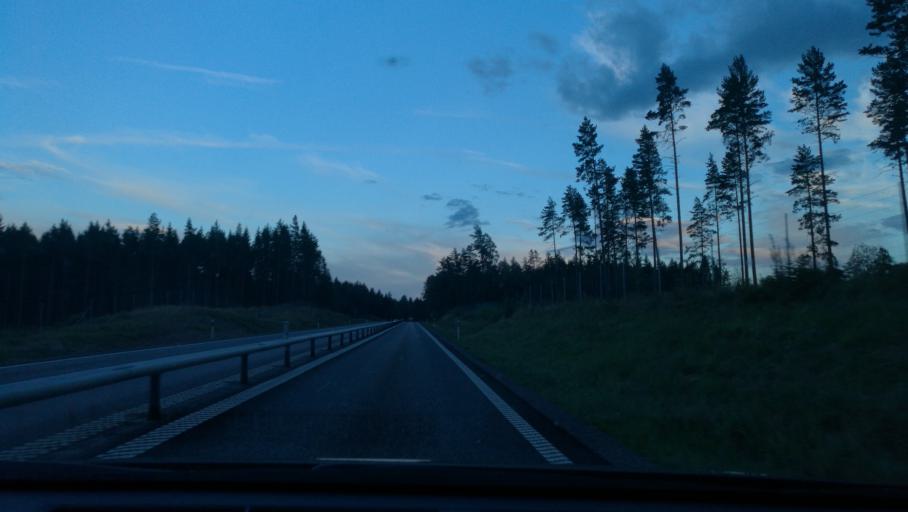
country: SE
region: Soedermanland
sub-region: Katrineholms Kommun
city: Katrineholm
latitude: 58.8631
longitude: 16.2005
